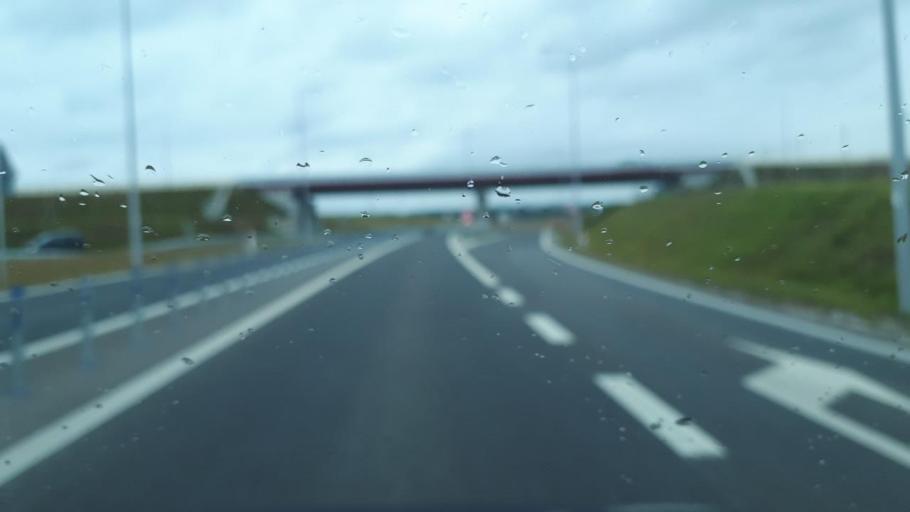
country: PL
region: Greater Poland Voivodeship
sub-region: Powiat kepinski
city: Baranow
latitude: 51.2551
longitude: 18.0153
